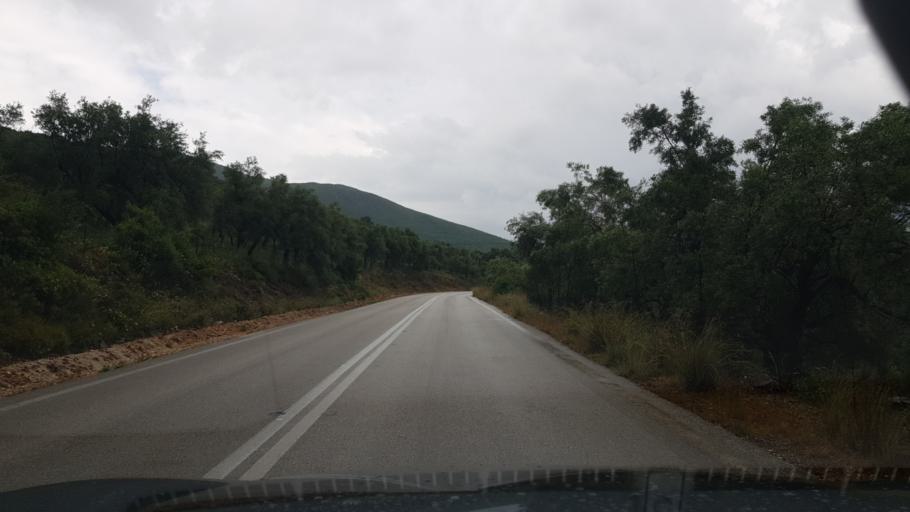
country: GR
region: Ionian Islands
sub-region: Lefkada
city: Nidri
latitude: 38.6410
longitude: 20.6751
